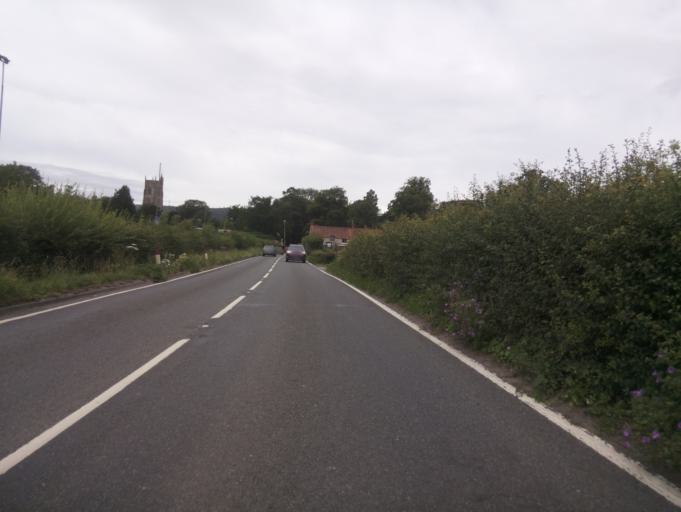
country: GB
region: England
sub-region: Somerset
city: Cheddar
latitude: 51.2718
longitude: -2.7735
